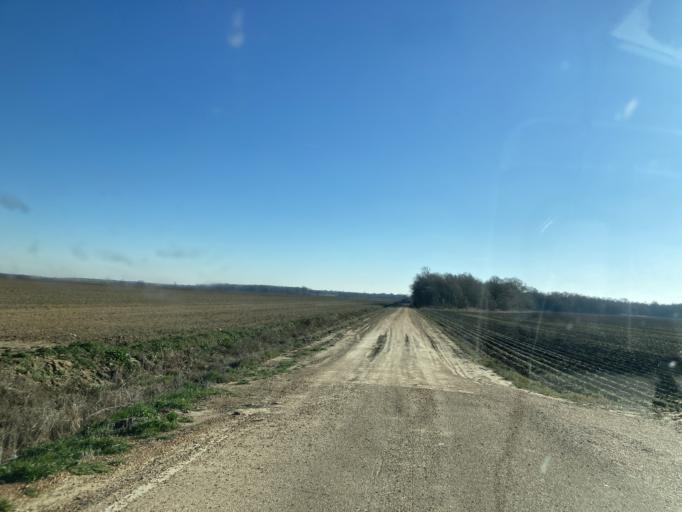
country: US
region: Mississippi
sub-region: Yazoo County
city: Yazoo City
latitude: 32.9373
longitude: -90.5865
